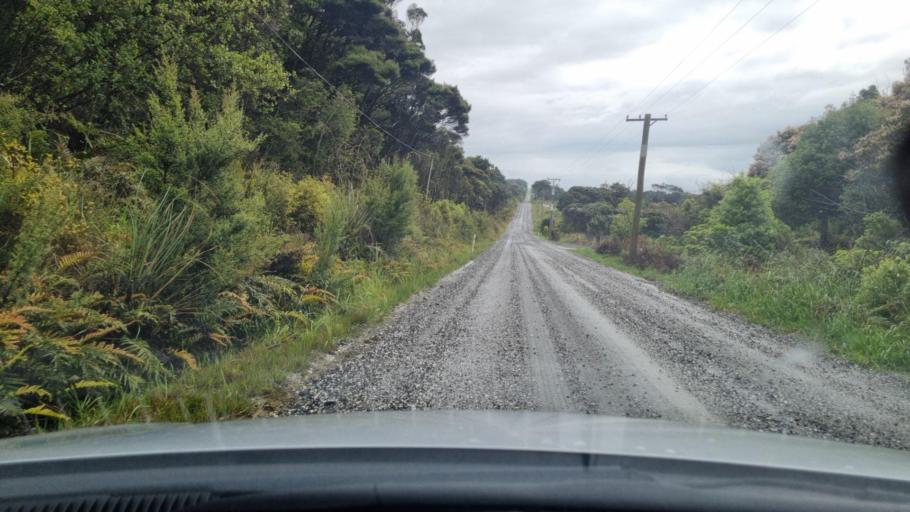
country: NZ
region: Southland
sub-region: Invercargill City
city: Bluff
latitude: -46.5392
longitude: 168.2645
